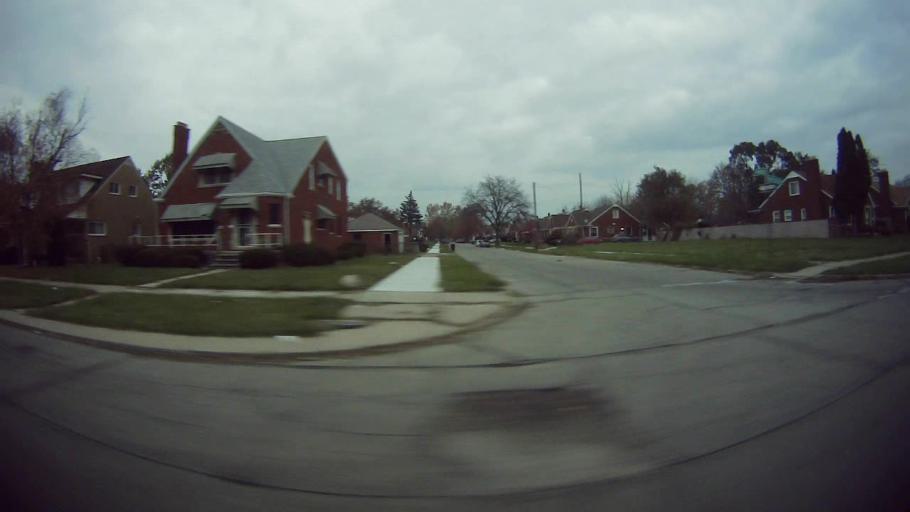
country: US
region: Michigan
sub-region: Macomb County
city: Warren
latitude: 42.4412
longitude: -83.0295
